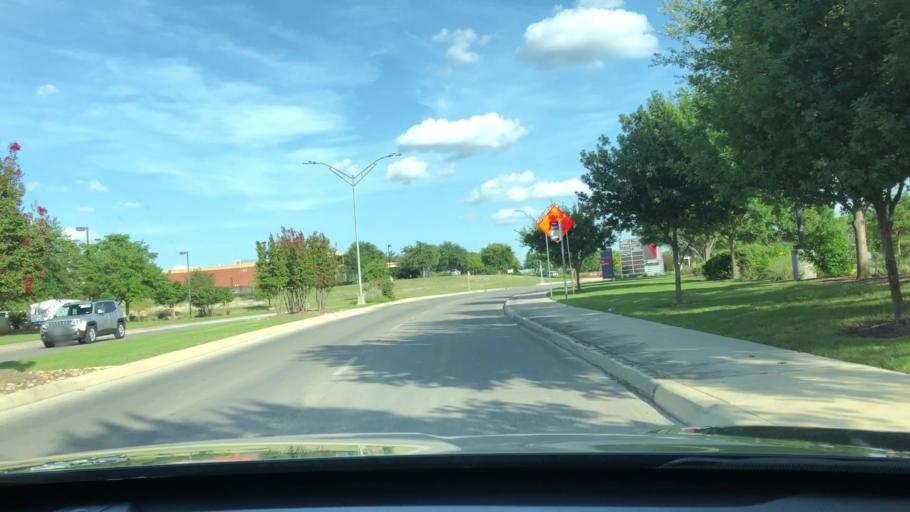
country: US
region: Texas
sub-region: Bexar County
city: Leon Valley
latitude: 29.5277
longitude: -98.5917
